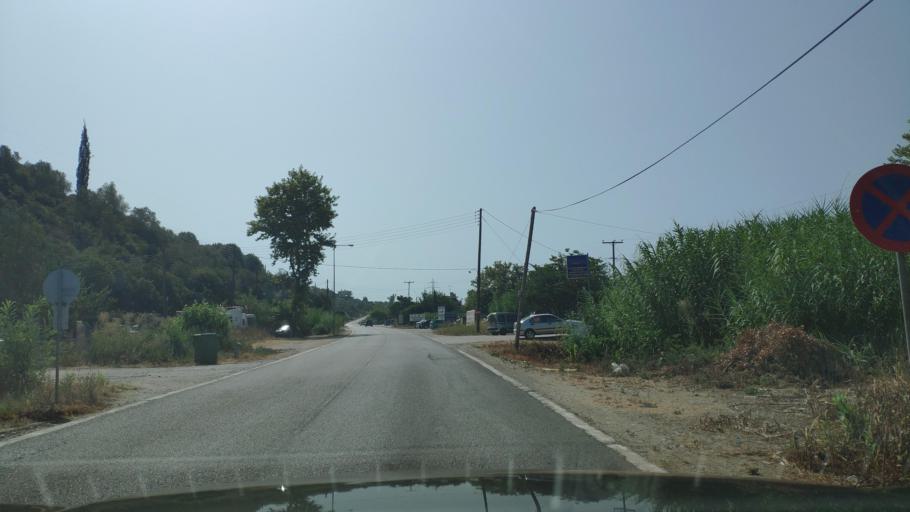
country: GR
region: Epirus
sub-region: Nomos Artas
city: Peta
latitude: 39.1621
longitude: 21.0196
